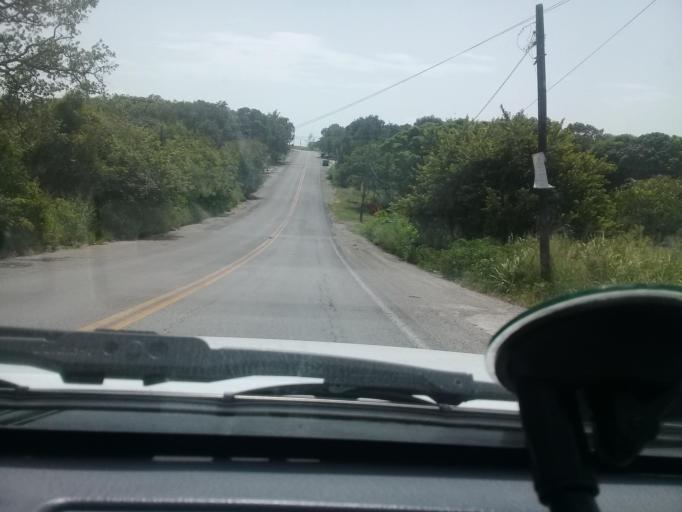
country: MX
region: Veracruz
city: Villa Cuauhtemoc
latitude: 22.2126
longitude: -97.8259
